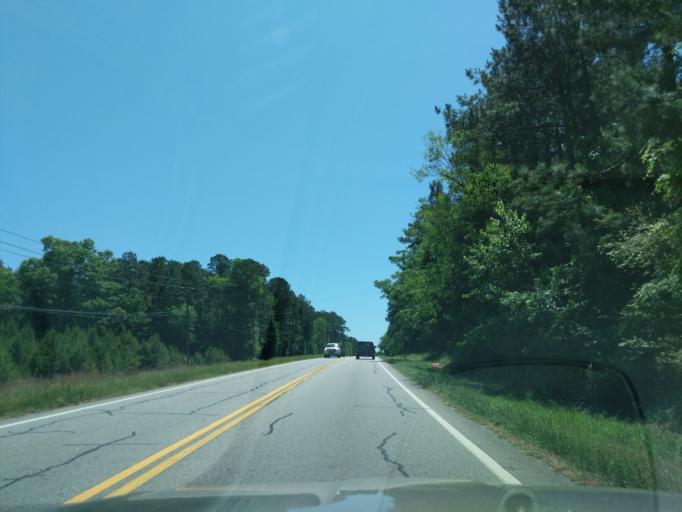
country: US
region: Georgia
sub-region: Columbia County
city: Evans
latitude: 33.5588
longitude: -82.1000
